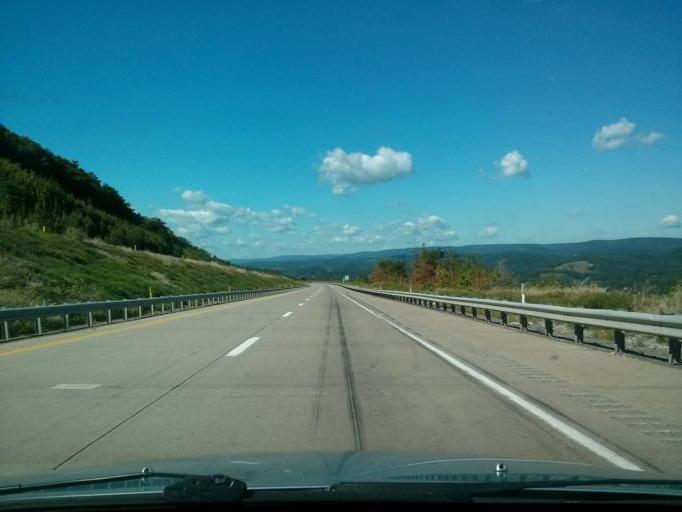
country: US
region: Pennsylvania
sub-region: Centre County
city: Stormstown
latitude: 40.8302
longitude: -77.9861
